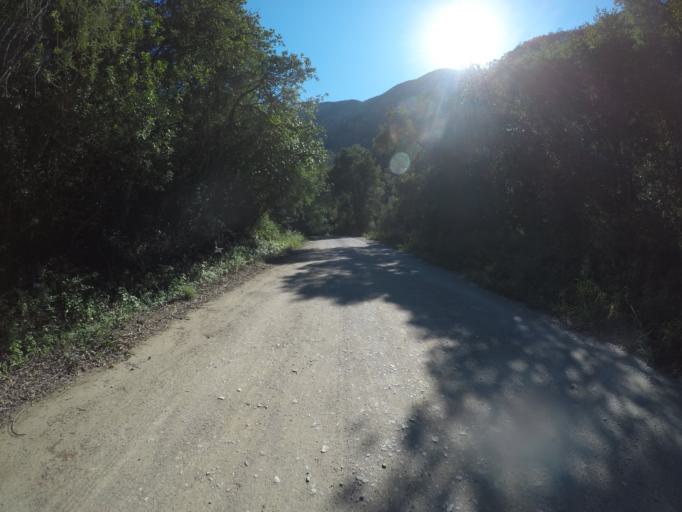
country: ZA
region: Eastern Cape
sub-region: Cacadu District Municipality
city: Kareedouw
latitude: -33.6551
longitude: 24.5235
